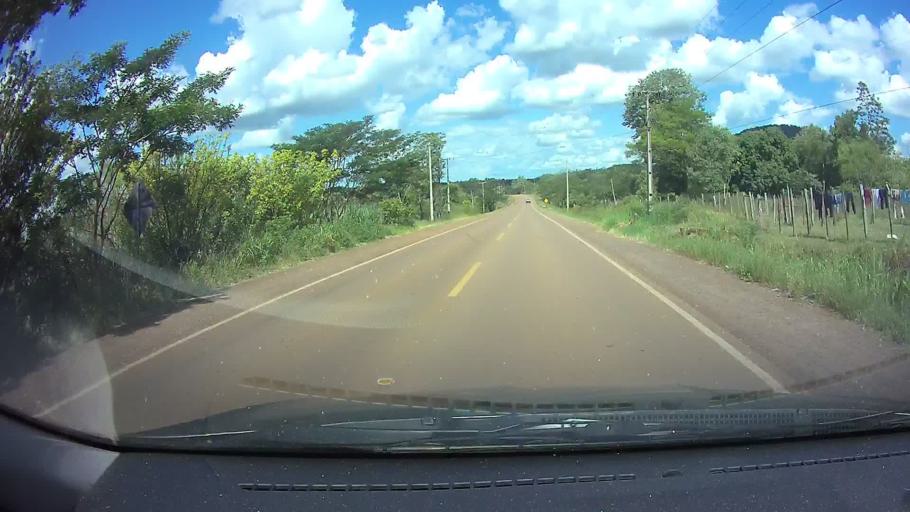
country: PY
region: Paraguari
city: La Colmena
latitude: -25.9155
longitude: -56.7424
